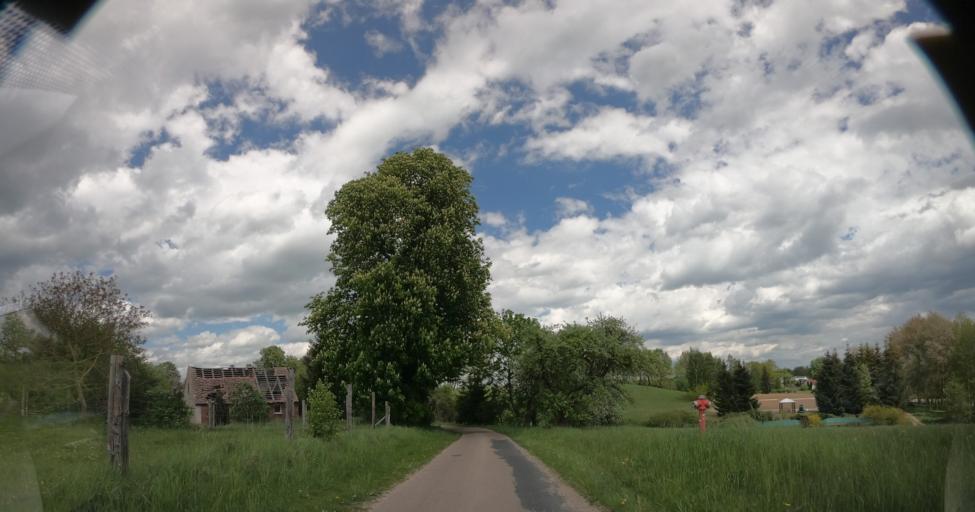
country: PL
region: West Pomeranian Voivodeship
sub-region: Powiat drawski
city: Drawsko Pomorskie
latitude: 53.5723
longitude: 15.7683
